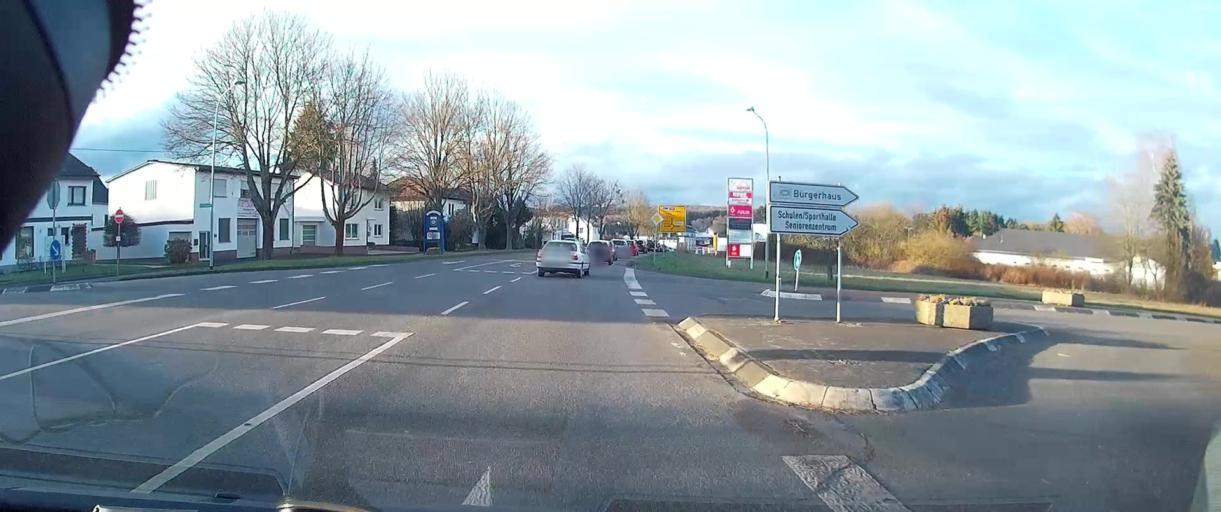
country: DE
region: Rheinland-Pfalz
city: Wirges
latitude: 50.4688
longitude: 7.7970
